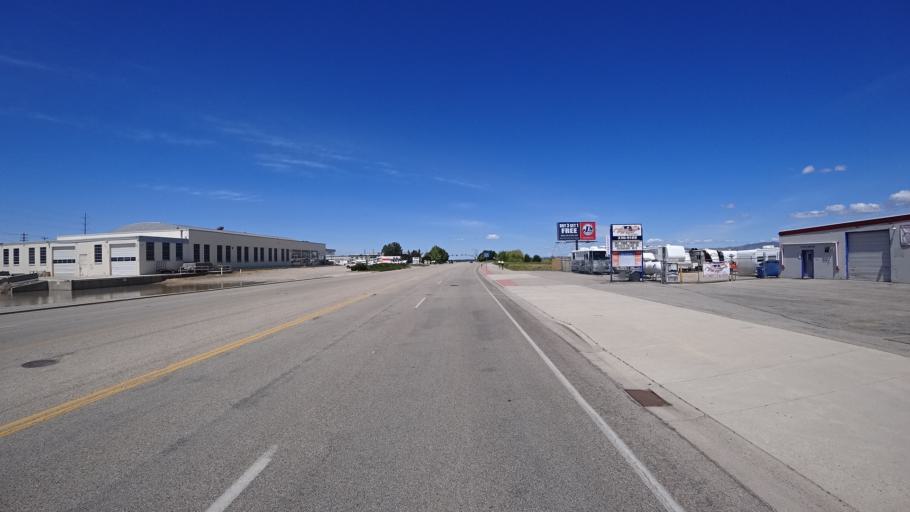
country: US
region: Idaho
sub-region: Ada County
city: Boise
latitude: 43.5613
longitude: -116.1698
